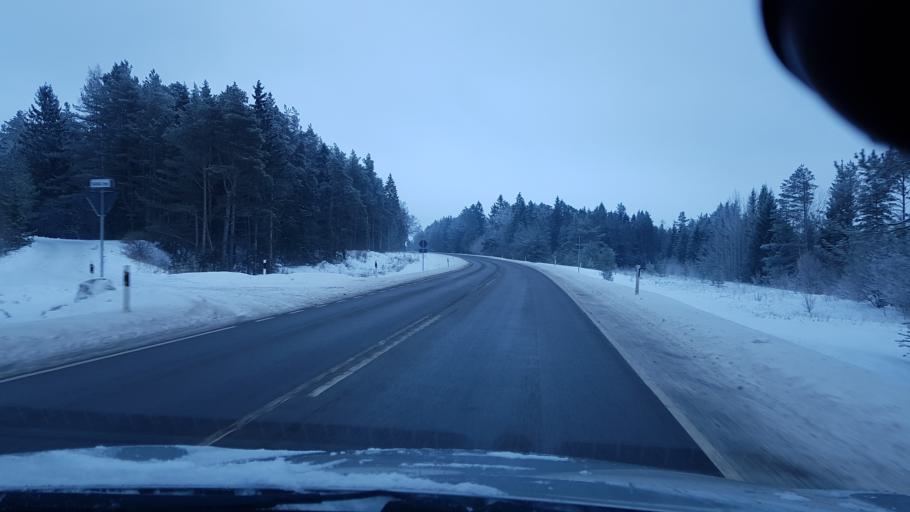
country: EE
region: Harju
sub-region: Keila linn
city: Keila
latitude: 59.3326
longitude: 24.2913
